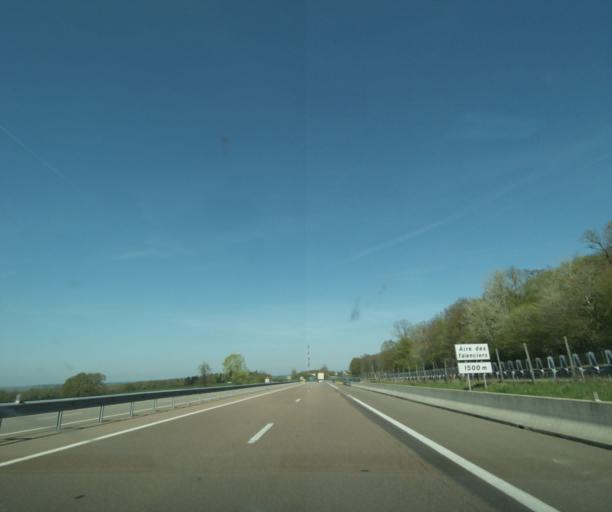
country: FR
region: Bourgogne
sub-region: Departement de la Nievre
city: Challuy
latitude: 46.9259
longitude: 3.1615
